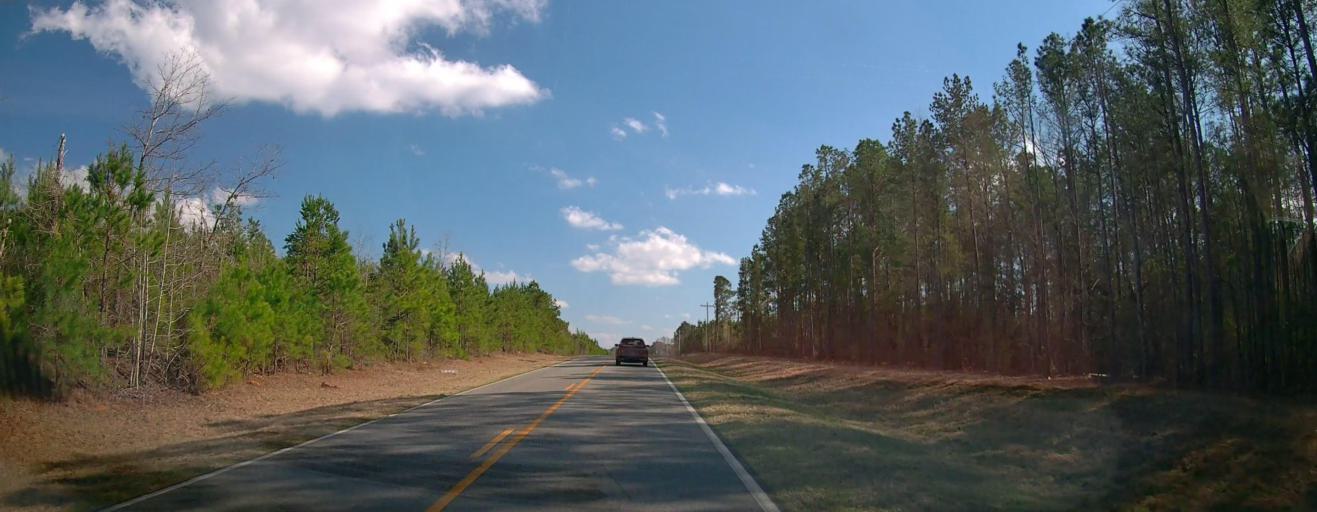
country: US
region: Georgia
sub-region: Laurens County
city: Dublin
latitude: 32.6024
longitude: -83.0745
